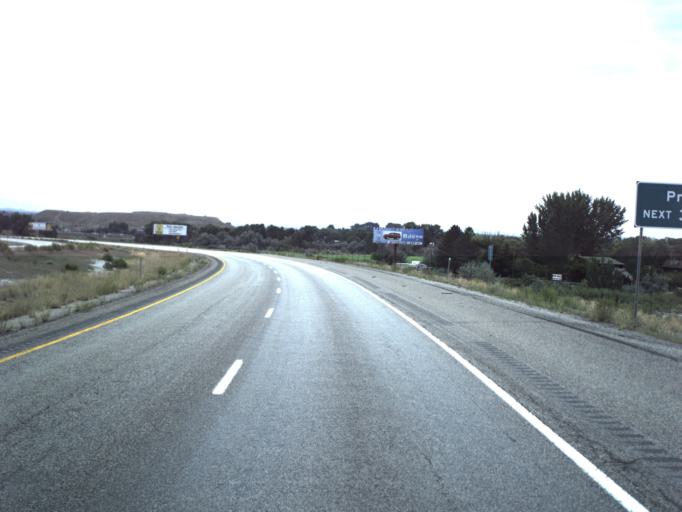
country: US
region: Utah
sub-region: Carbon County
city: Carbonville
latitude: 39.6179
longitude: -110.8539
